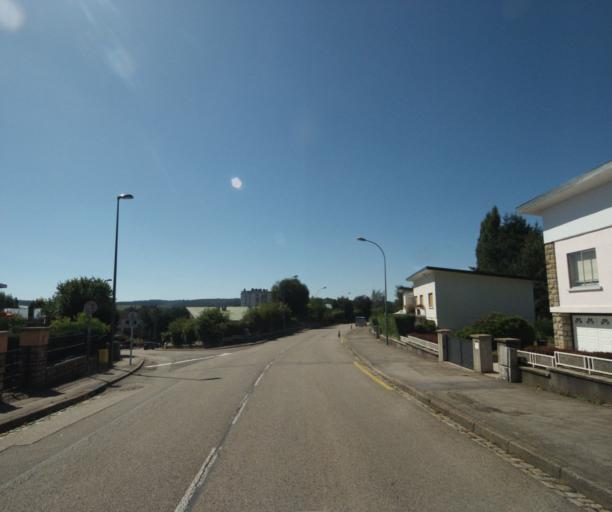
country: FR
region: Lorraine
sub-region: Departement des Vosges
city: Epinal
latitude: 48.1831
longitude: 6.4576
